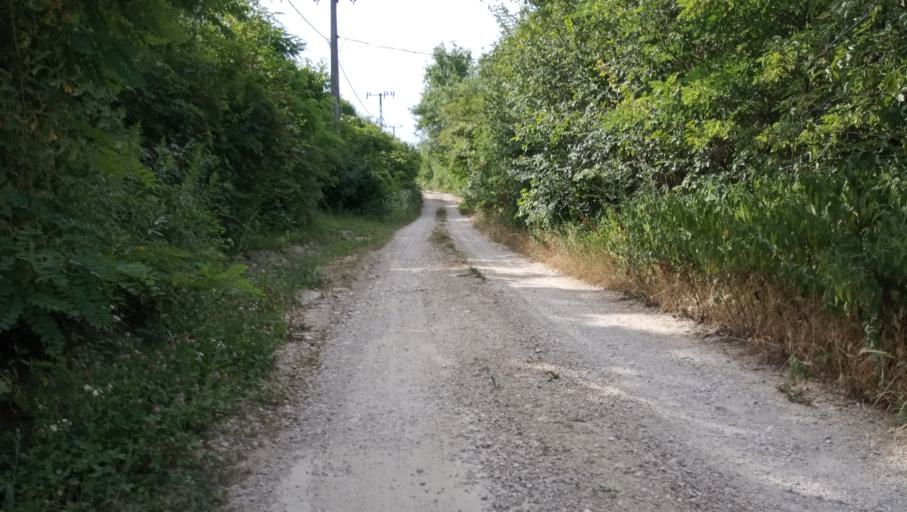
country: HU
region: Veszprem
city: Balatonkenese
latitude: 47.0412
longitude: 18.0923
